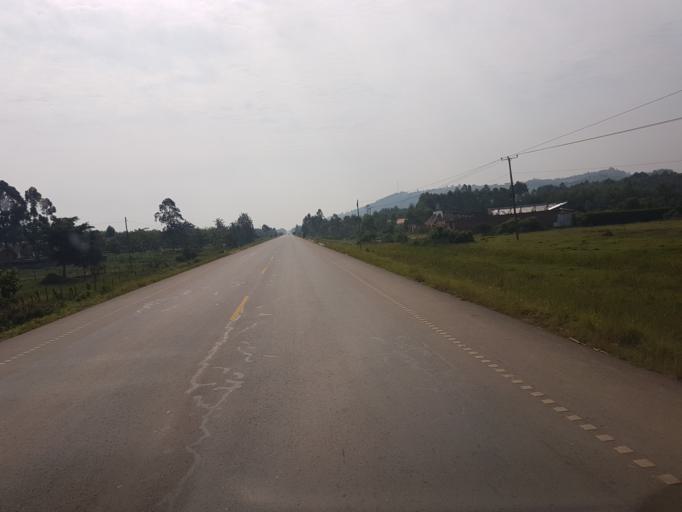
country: UG
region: Western Region
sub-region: Sheema District
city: Kibingo
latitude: -0.6458
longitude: 30.4938
